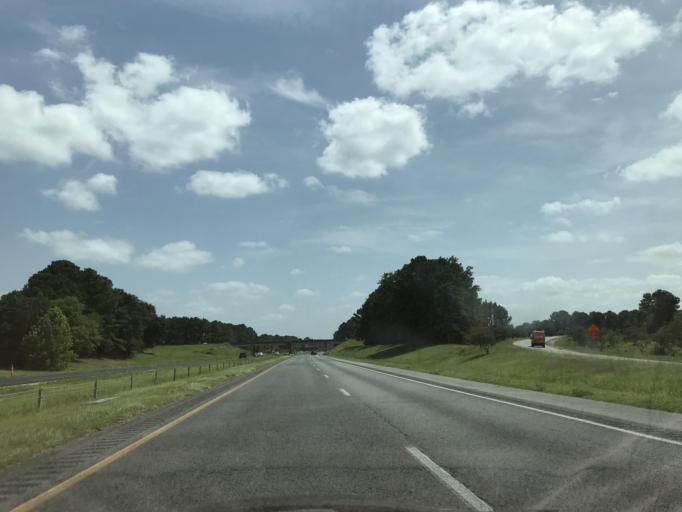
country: US
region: North Carolina
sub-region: Duplin County
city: Kenansville
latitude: 34.9198
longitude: -78.0265
